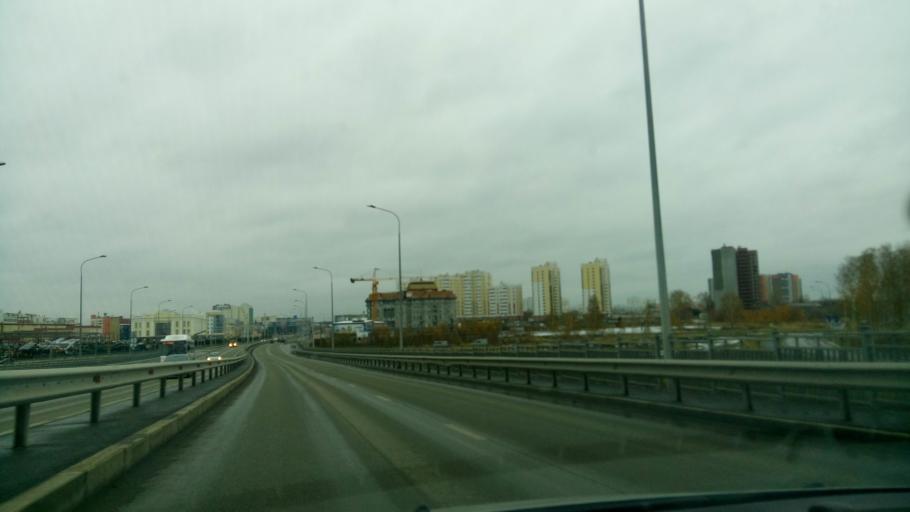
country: RU
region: Sverdlovsk
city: Verkhnyaya Pyshma
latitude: 56.9607
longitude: 60.5874
